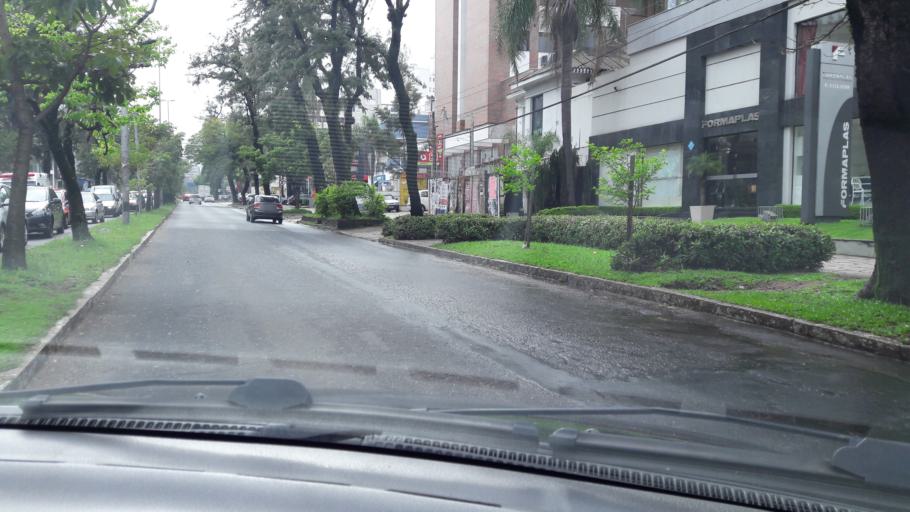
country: BR
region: Rio Grande do Sul
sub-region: Porto Alegre
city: Porto Alegre
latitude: -30.0313
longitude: -51.2027
